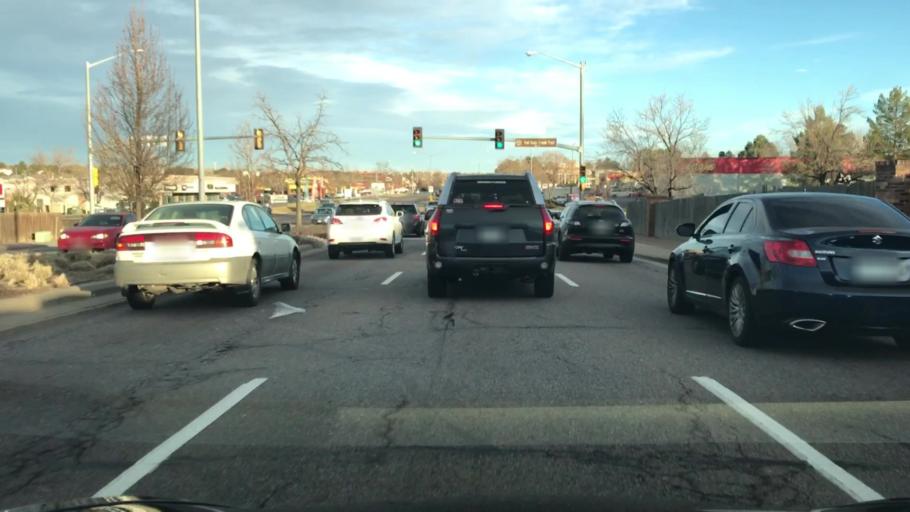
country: US
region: Colorado
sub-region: Adams County
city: Aurora
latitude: 39.6736
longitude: -104.7955
